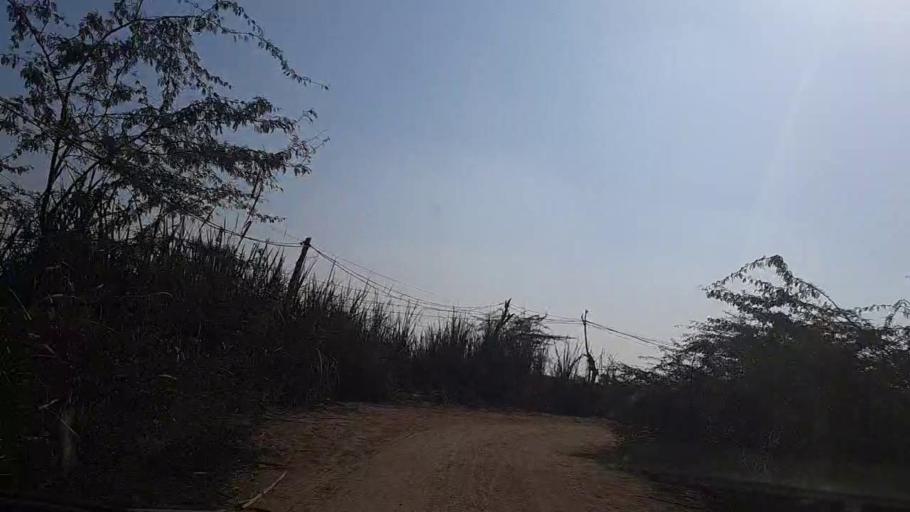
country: PK
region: Sindh
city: Sakrand
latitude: 26.0850
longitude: 68.3704
